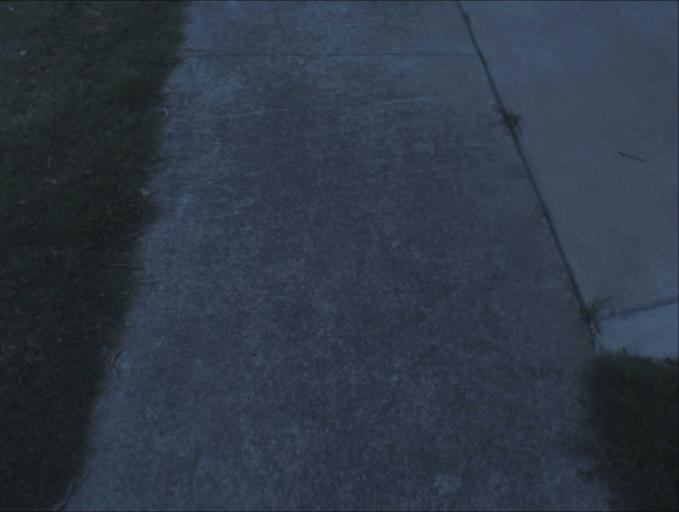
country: AU
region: Queensland
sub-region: Logan
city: Windaroo
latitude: -27.7207
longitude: 153.1861
